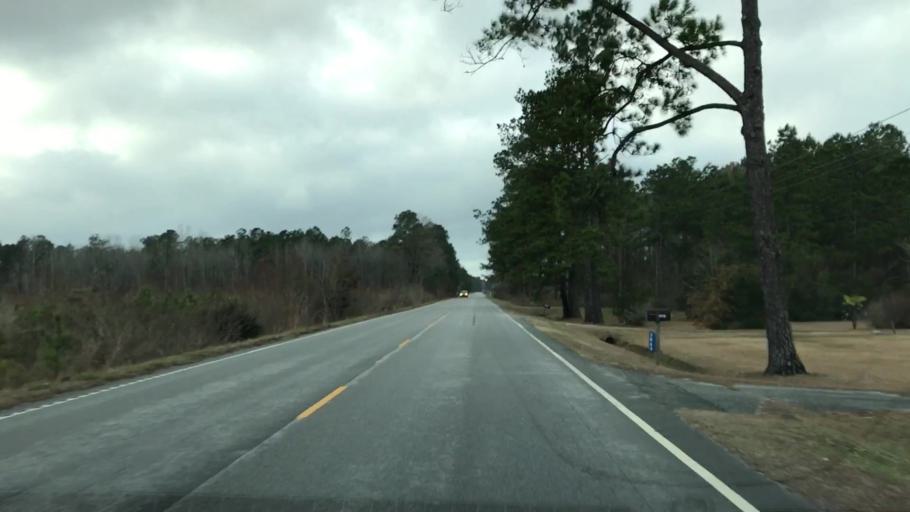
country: US
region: South Carolina
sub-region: Berkeley County
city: Saint Stephen
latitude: 33.2832
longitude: -79.7399
